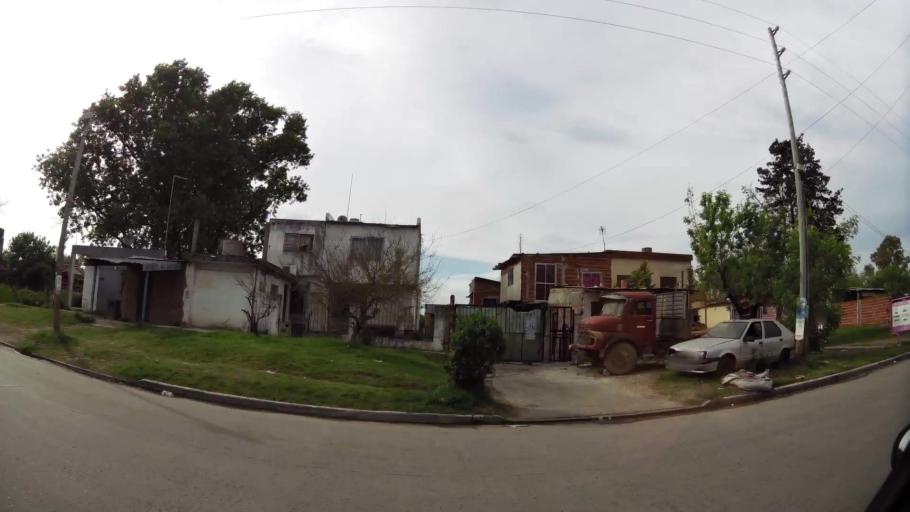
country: AR
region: Buenos Aires
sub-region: Partido de Quilmes
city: Quilmes
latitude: -34.7116
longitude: -58.2255
